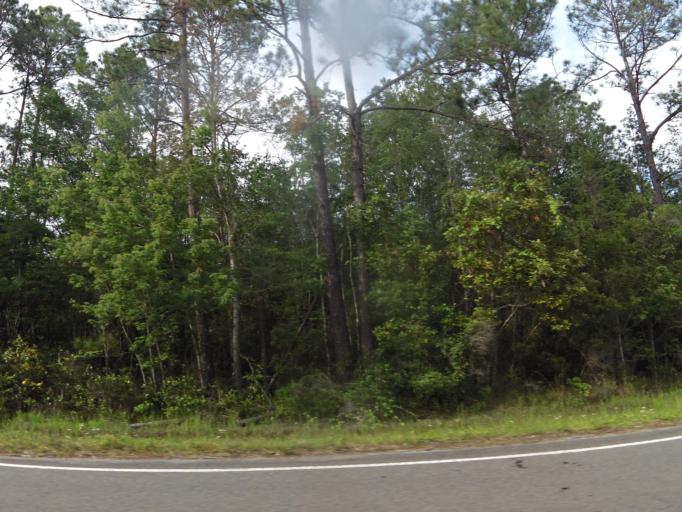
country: US
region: Georgia
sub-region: Camden County
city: Kingsland
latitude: 30.6926
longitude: -81.7061
